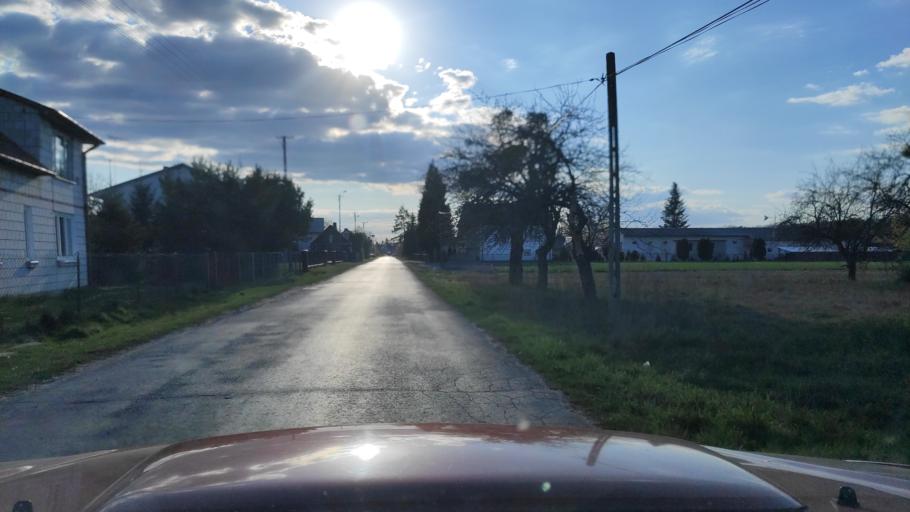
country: PL
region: Masovian Voivodeship
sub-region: Powiat zwolenski
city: Zwolen
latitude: 51.3843
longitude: 21.5679
